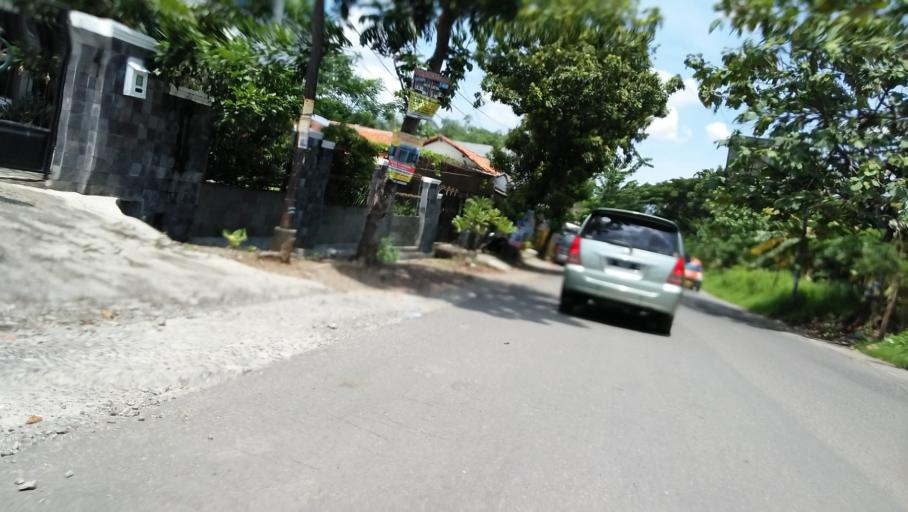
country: ID
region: Central Java
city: Mranggen
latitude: -7.0426
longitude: 110.4667
